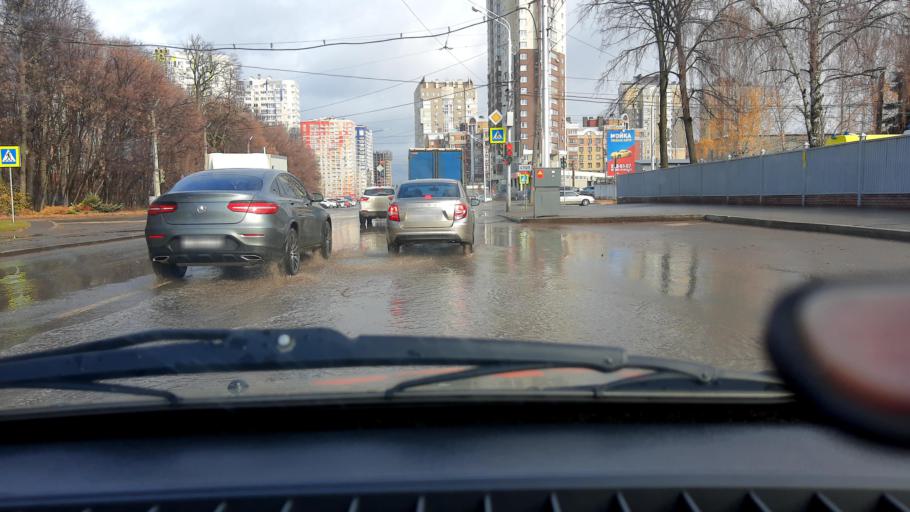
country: RU
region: Bashkortostan
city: Ufa
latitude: 54.7658
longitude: 56.0088
